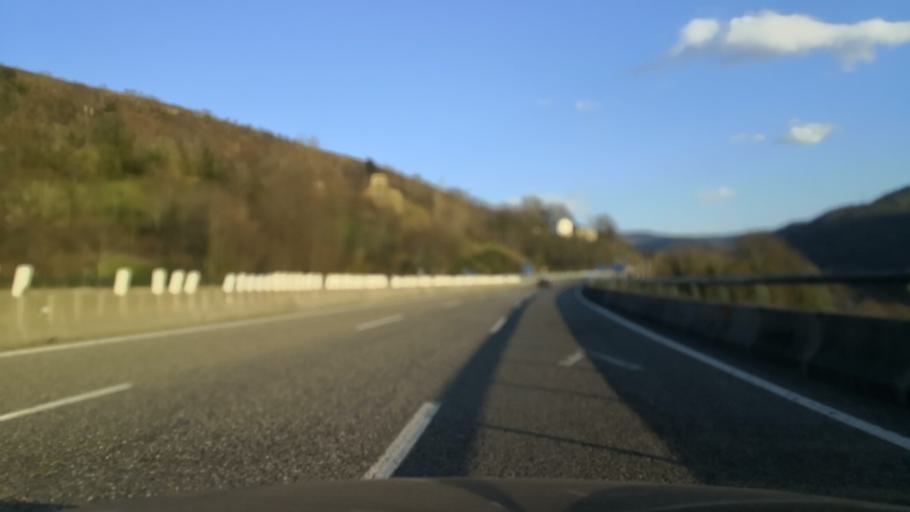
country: ES
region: Galicia
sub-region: Provincia de Lugo
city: San Roman
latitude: 42.7618
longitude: -7.0784
